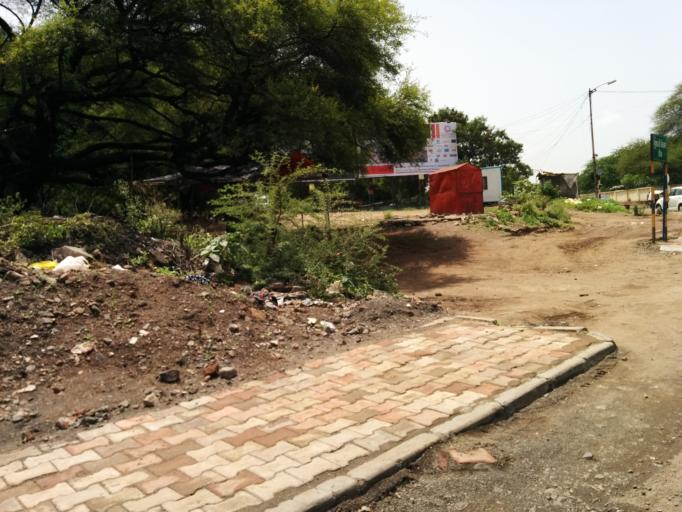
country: IN
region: Maharashtra
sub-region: Pune Division
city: Shivaji Nagar
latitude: 18.5392
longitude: 73.9038
